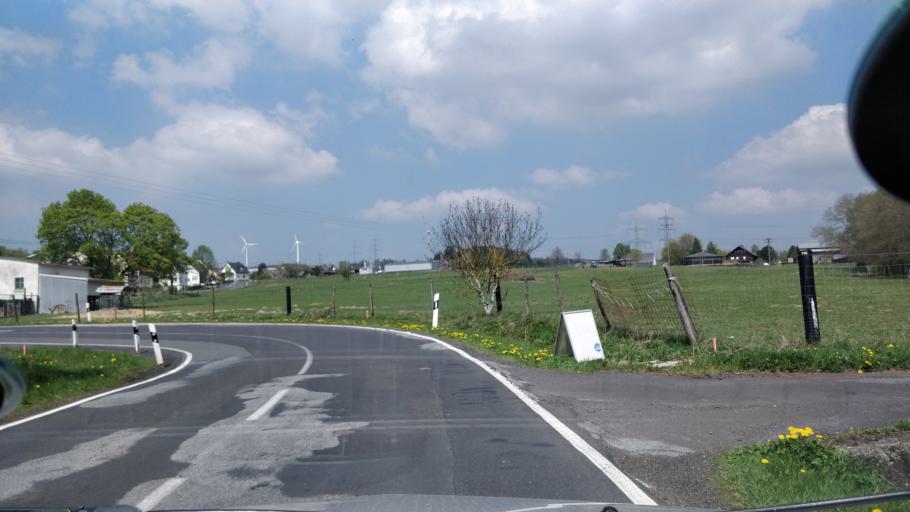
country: DE
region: Rheinland-Pfalz
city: Fehl-Ritzhausen
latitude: 50.6393
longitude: 8.0085
